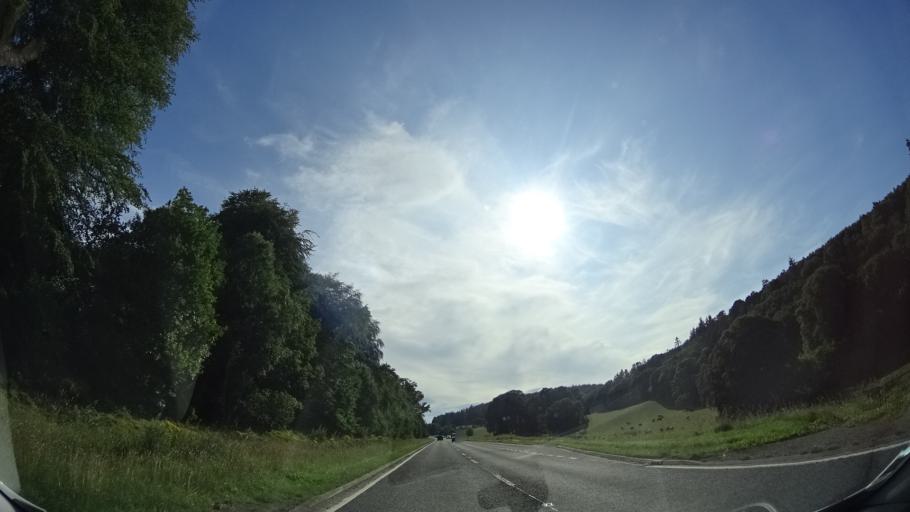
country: GB
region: Scotland
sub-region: Highland
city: Conon Bridge
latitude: 57.5714
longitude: -4.4584
